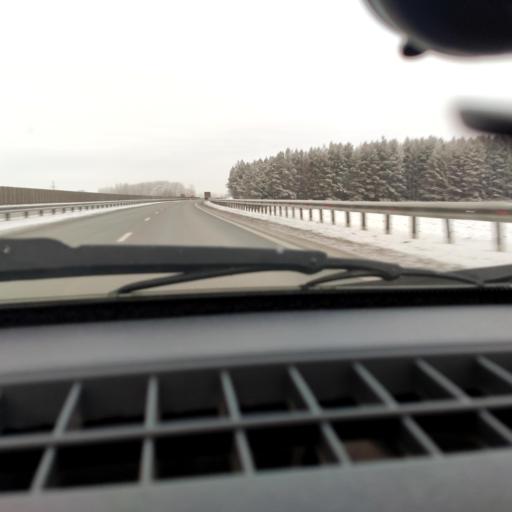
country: RU
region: Bashkortostan
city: Asanovo
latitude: 54.9845
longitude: 55.5258
